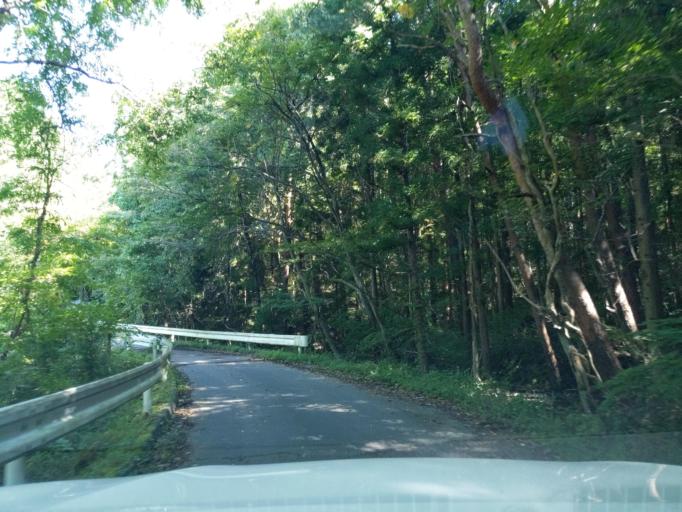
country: JP
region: Fukushima
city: Koriyama
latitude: 37.3991
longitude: 140.2384
